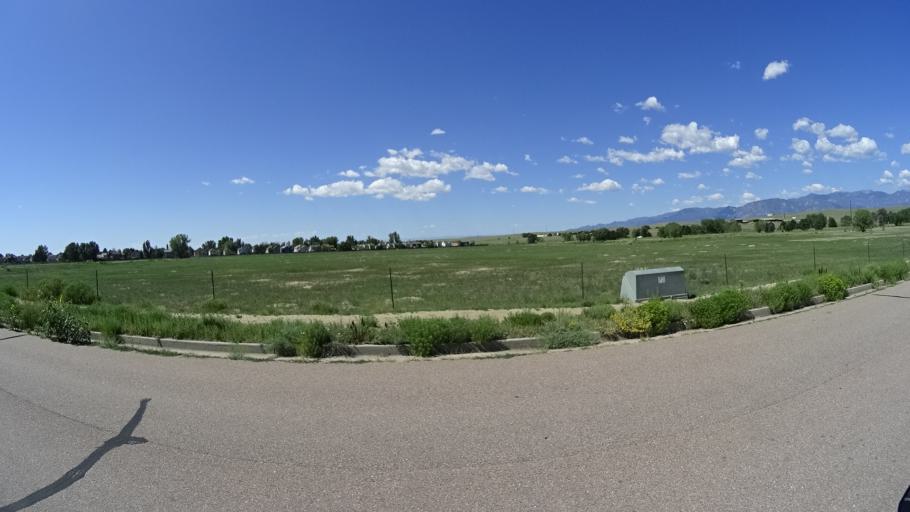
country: US
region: Colorado
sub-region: El Paso County
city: Security-Widefield
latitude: 38.7726
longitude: -104.6549
